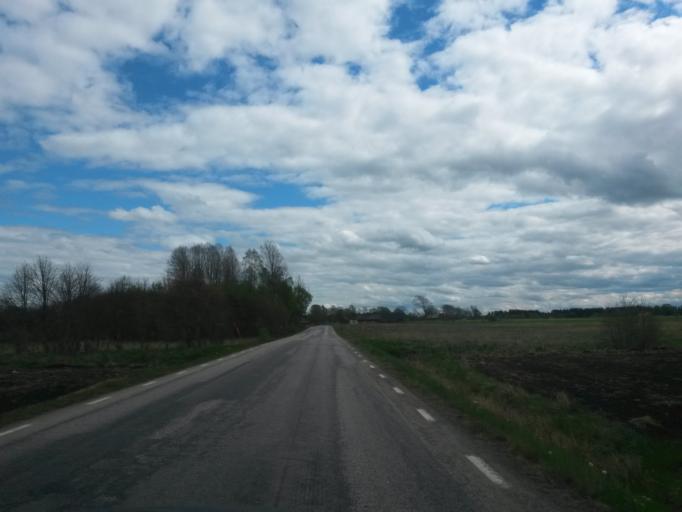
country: SE
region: Vaestra Goetaland
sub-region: Essunga Kommun
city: Nossebro
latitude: 58.1440
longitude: 12.7648
